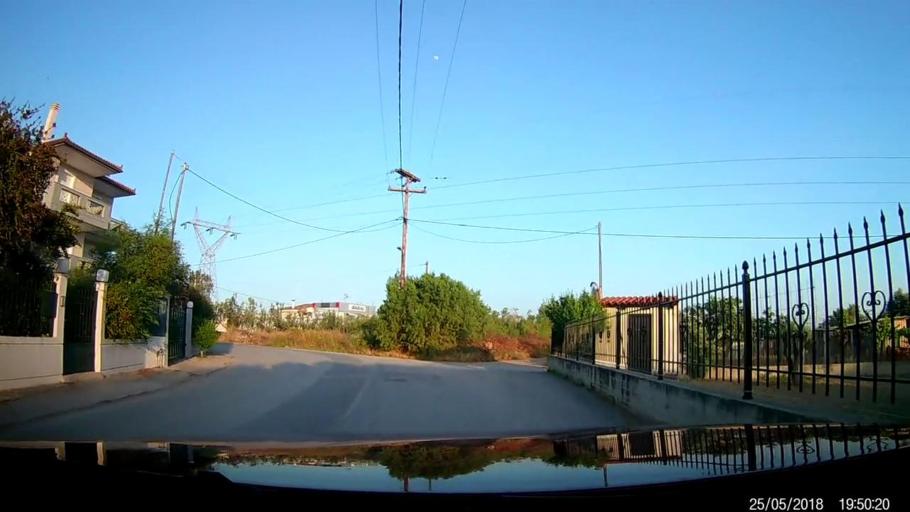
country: GR
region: Central Greece
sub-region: Nomos Evvoias
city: Ayios Nikolaos
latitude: 38.4077
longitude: 23.6407
